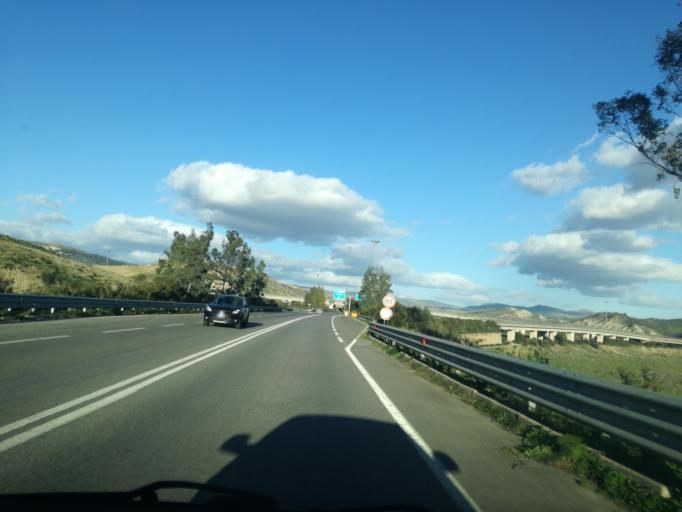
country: IT
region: Sicily
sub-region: Enna
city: Pietraperzia
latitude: 37.4537
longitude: 14.1045
